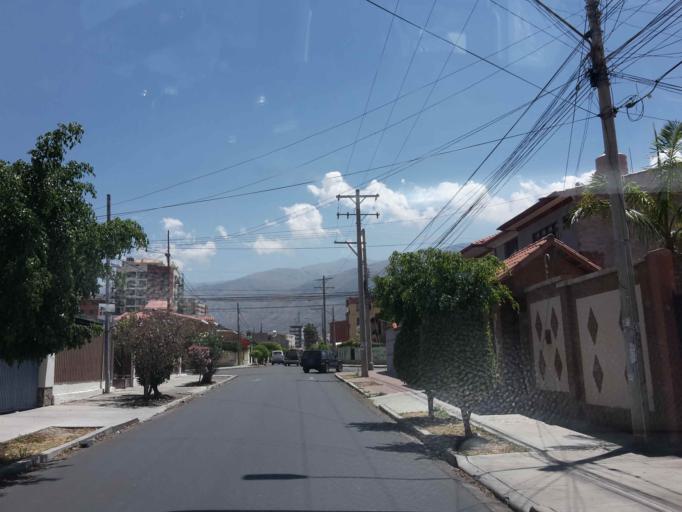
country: BO
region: Cochabamba
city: Cochabamba
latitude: -17.3770
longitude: -66.1657
